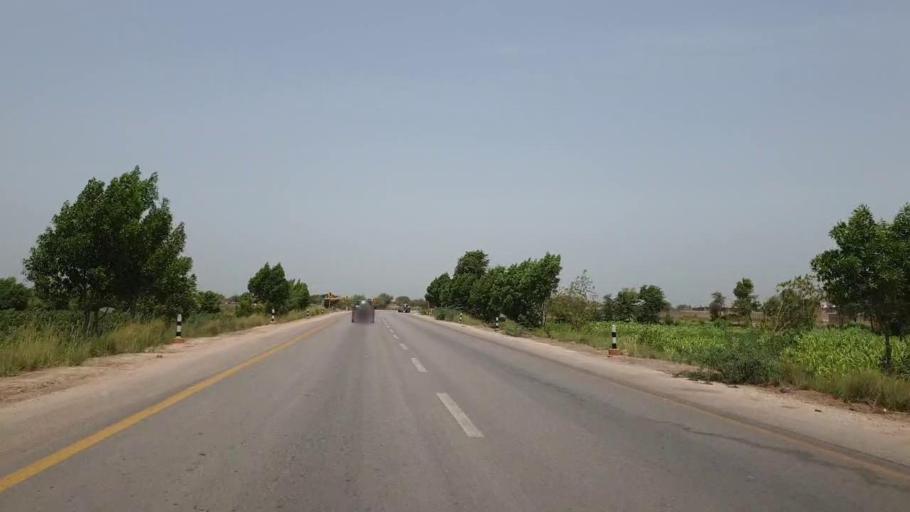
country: PK
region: Sindh
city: Nawabshah
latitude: 26.2140
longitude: 68.5103
